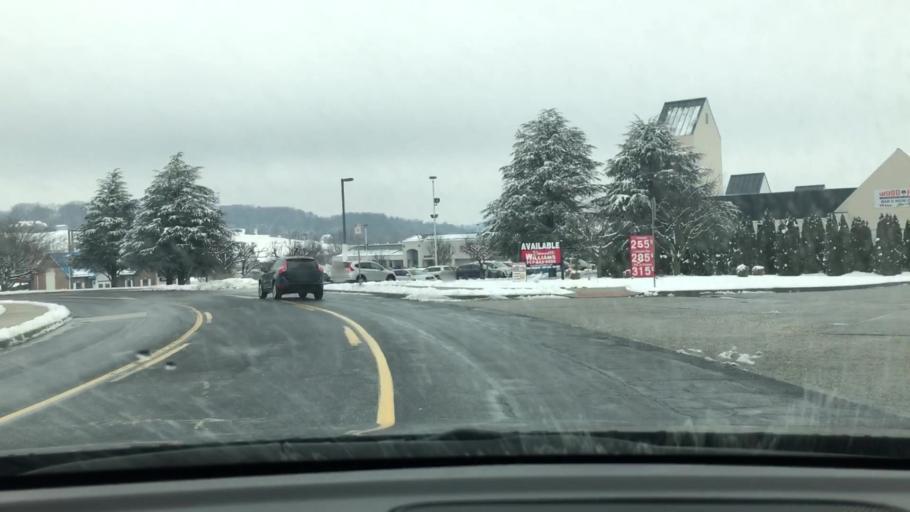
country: US
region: Pennsylvania
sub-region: York County
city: Spry
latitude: 39.9321
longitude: -76.6838
